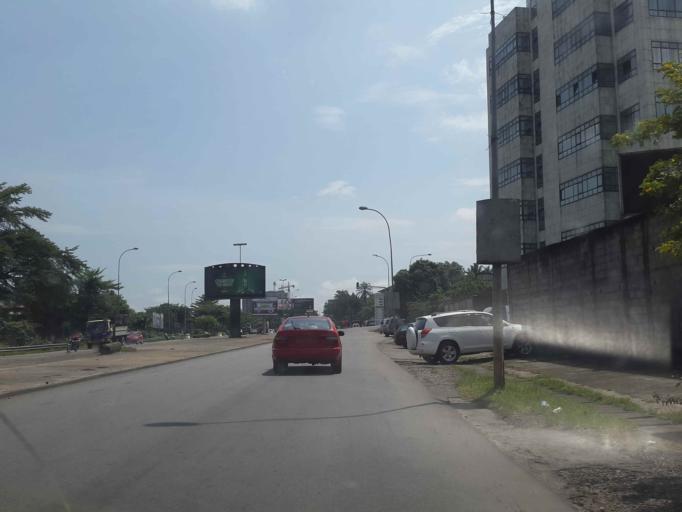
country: CM
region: Littoral
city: Douala
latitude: 4.0350
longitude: 9.6898
